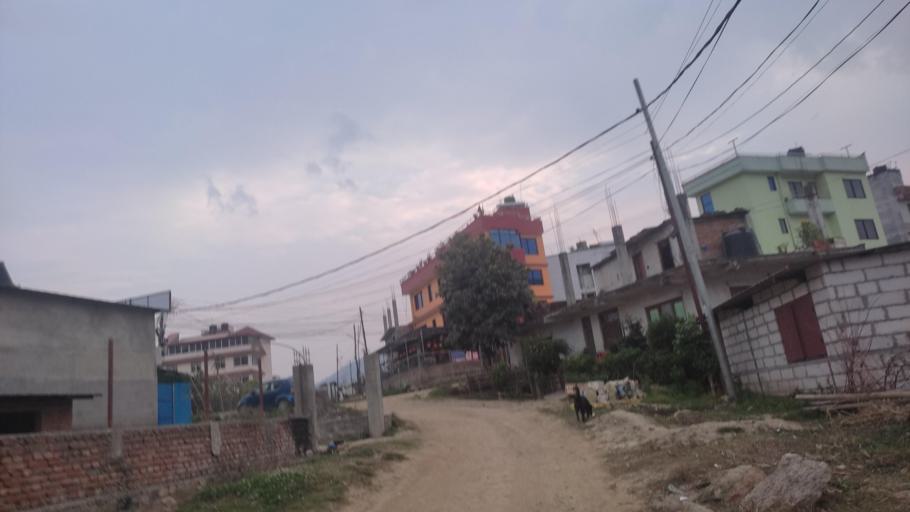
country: NP
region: Central Region
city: Kirtipur
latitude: 27.6603
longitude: 85.2872
